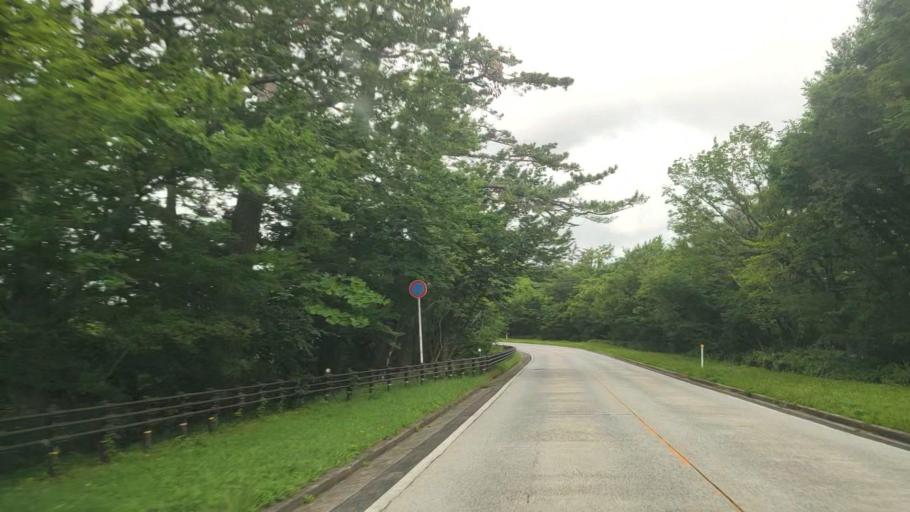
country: JP
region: Tottori
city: Yonago
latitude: 35.3956
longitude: 133.5248
